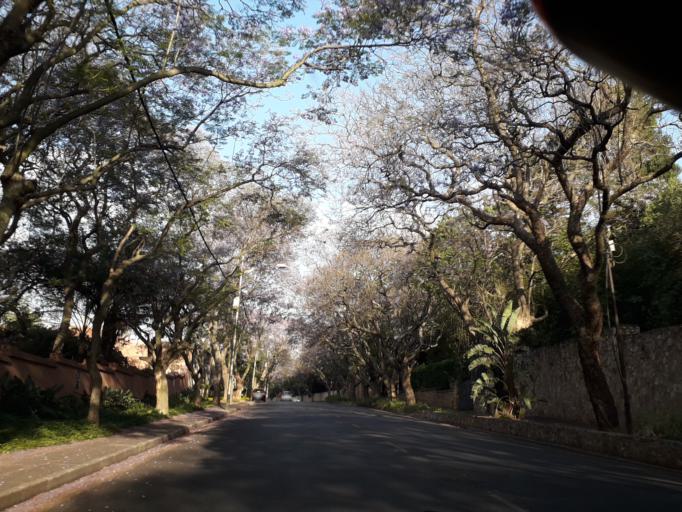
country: ZA
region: Gauteng
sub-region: City of Johannesburg Metropolitan Municipality
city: Johannesburg
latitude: -26.1706
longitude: 28.0583
